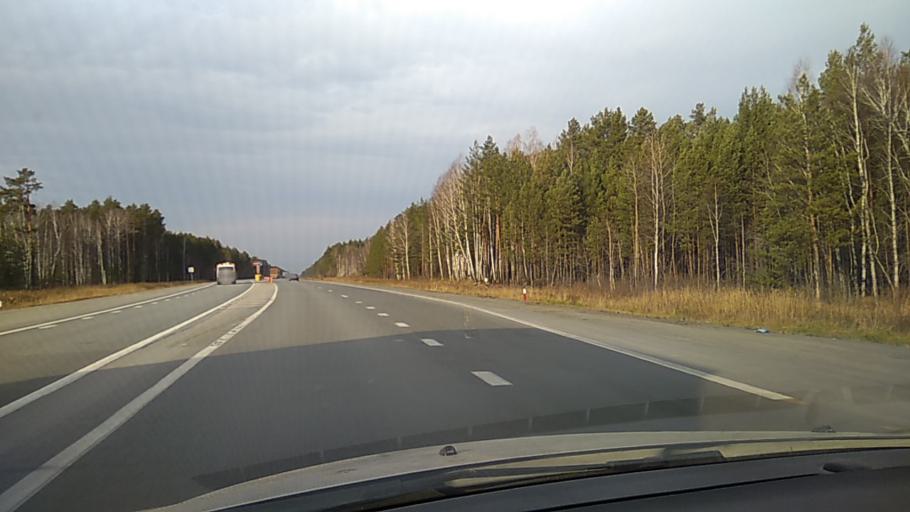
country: RU
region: Sverdlovsk
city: Lugovskoy
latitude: 57.0755
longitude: 64.5258
